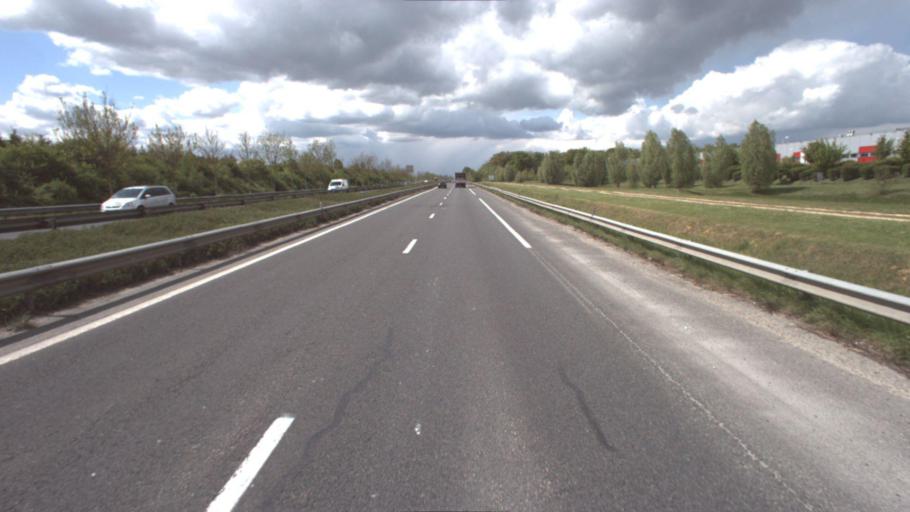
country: FR
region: Ile-de-France
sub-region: Departement de Seine-et-Marne
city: Fontenay-Tresigny
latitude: 48.7220
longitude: 2.8372
